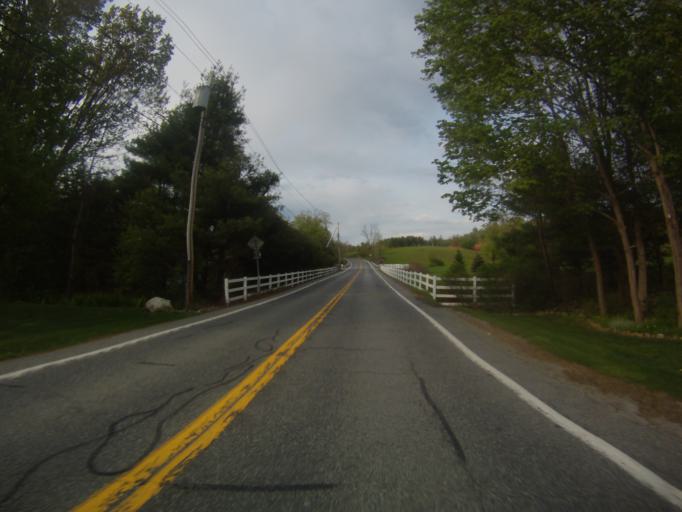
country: US
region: New York
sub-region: Warren County
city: Warrensburg
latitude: 43.7052
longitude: -73.7090
